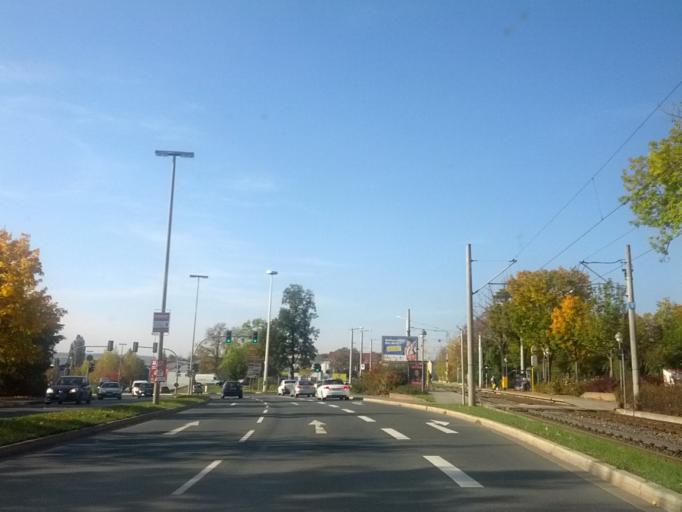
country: DE
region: Thuringia
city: Gera
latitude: 50.8962
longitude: 12.0774
